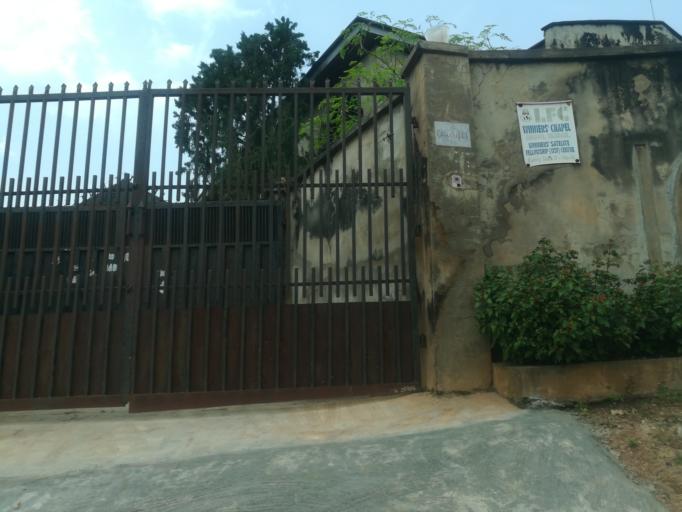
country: NG
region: Oyo
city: Moniya
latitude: 7.4524
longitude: 3.9583
